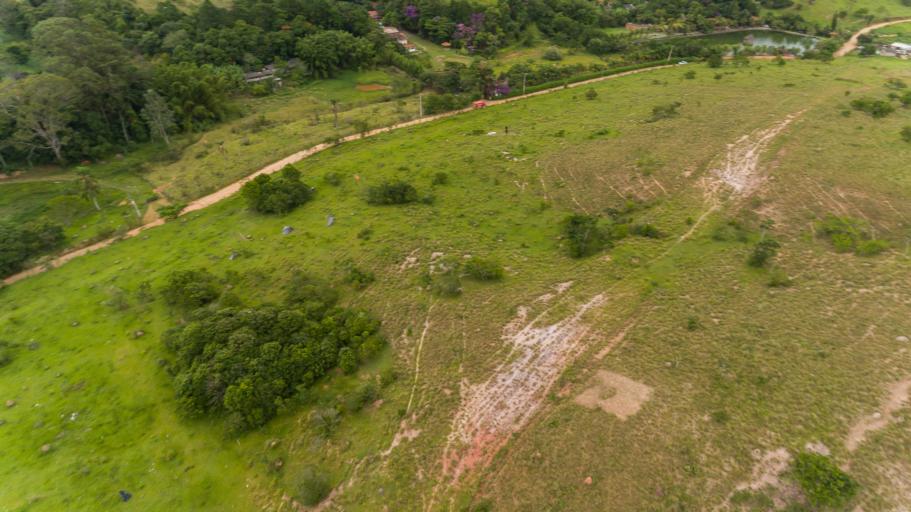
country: BR
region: Sao Paulo
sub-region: Jacarei
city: Jacarei
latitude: -23.3027
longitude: -45.9084
